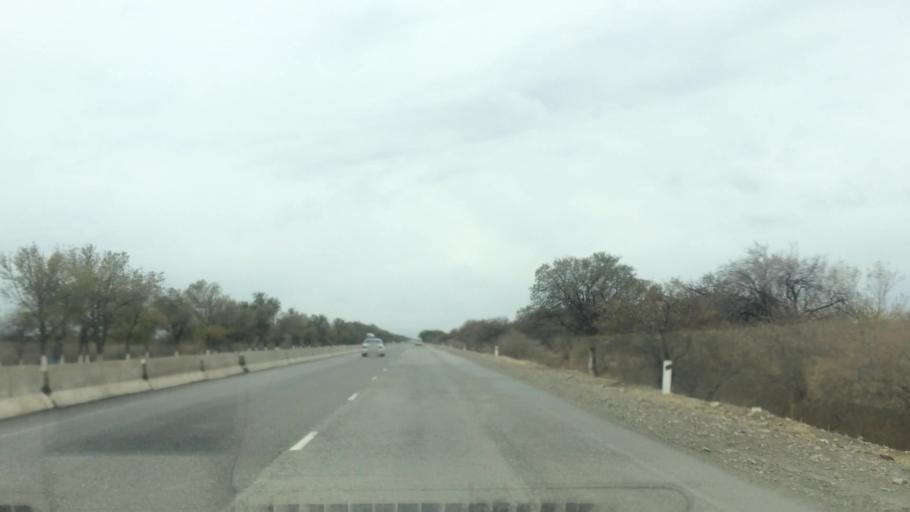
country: UZ
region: Samarqand
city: Bulung'ur
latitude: 39.8170
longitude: 67.3809
